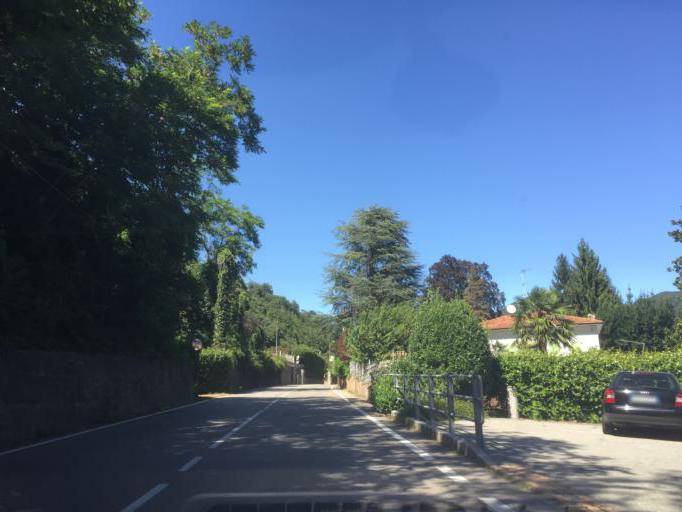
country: IT
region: Lombardy
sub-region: Provincia di Varese
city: Porto Ceresio
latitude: 45.9124
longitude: 8.8979
